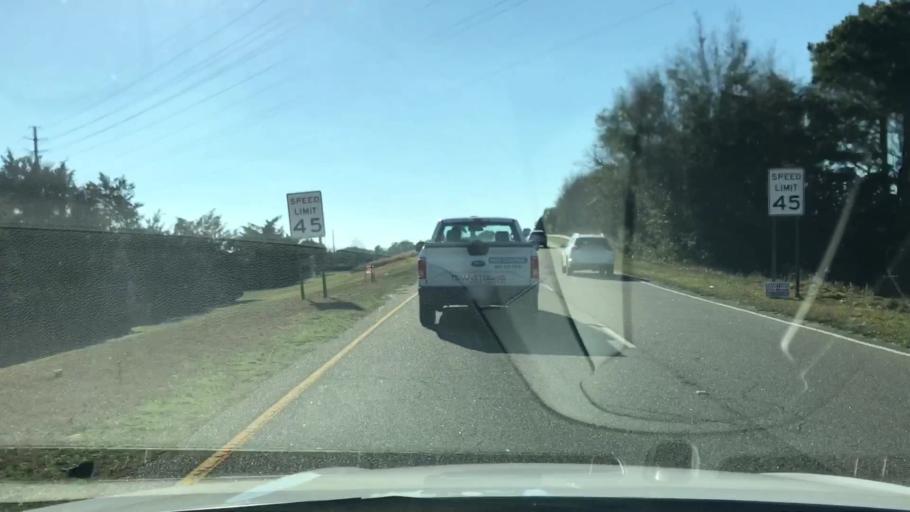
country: US
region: South Carolina
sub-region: Horry County
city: Garden City
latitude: 33.5754
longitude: -79.0272
